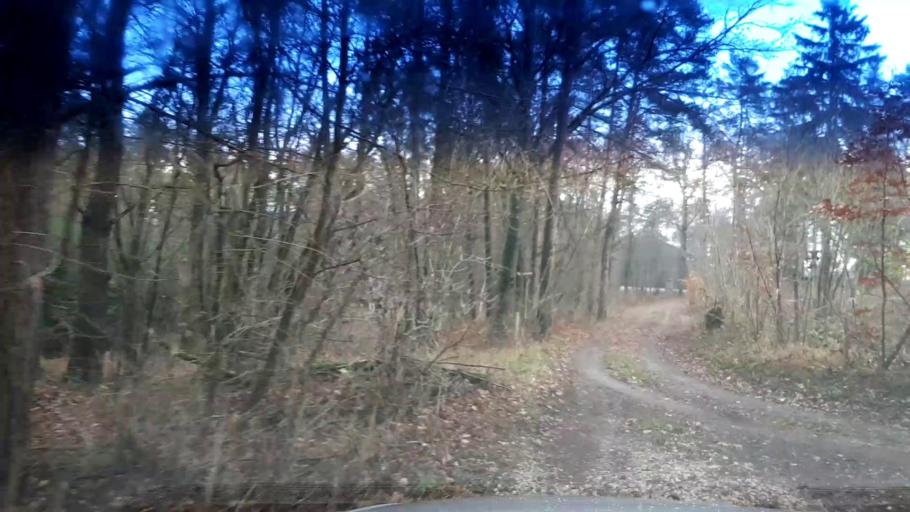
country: DE
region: Bavaria
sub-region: Upper Franconia
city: Poxdorf
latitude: 49.9365
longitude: 11.1070
